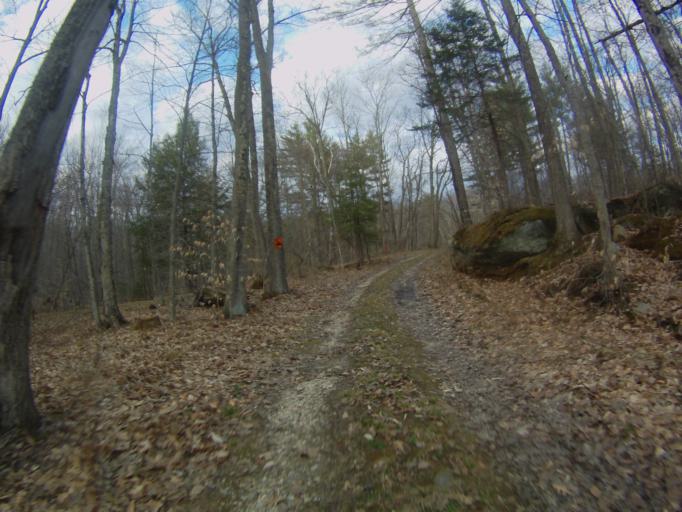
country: US
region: Vermont
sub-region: Rutland County
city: Brandon
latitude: 43.8438
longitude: -73.0352
